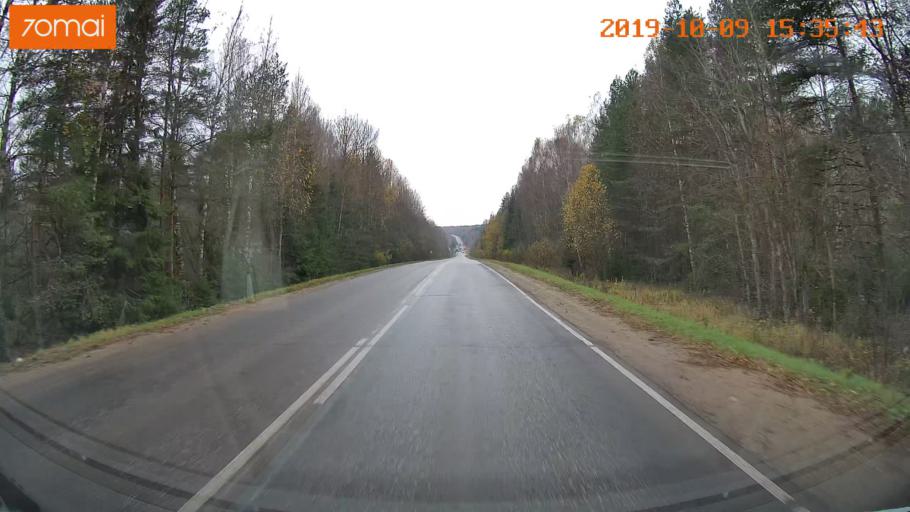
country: RU
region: Kostroma
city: Oktyabr'skiy
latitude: 57.9292
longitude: 41.2219
